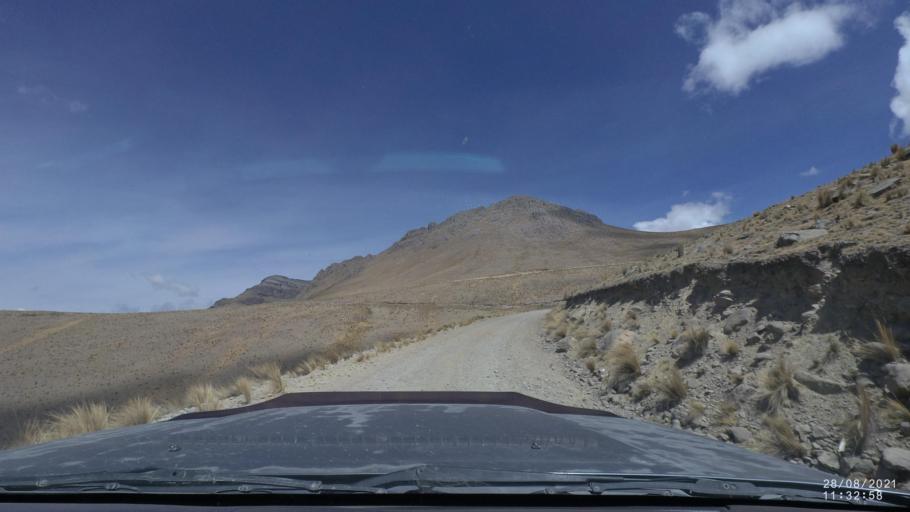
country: BO
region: Cochabamba
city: Sipe Sipe
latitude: -17.1840
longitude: -66.3691
